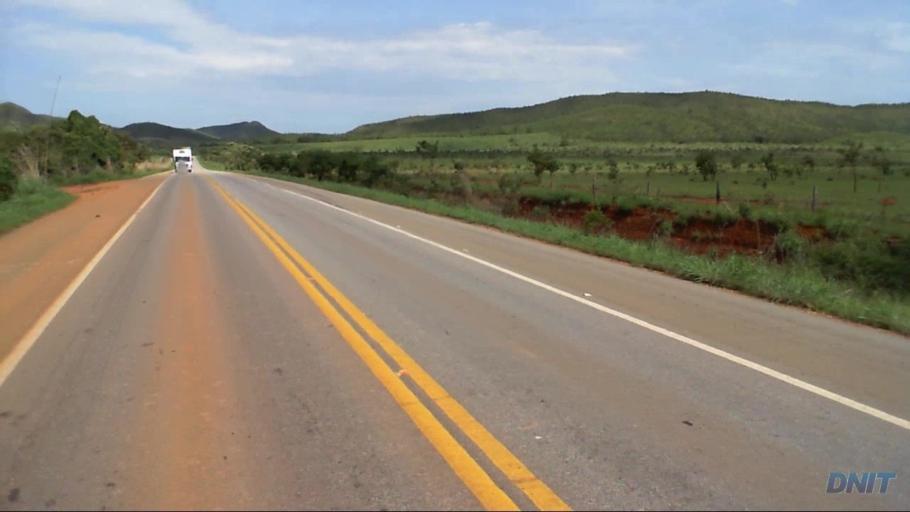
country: BR
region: Goias
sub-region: Barro Alto
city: Barro Alto
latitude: -15.1880
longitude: -48.7783
